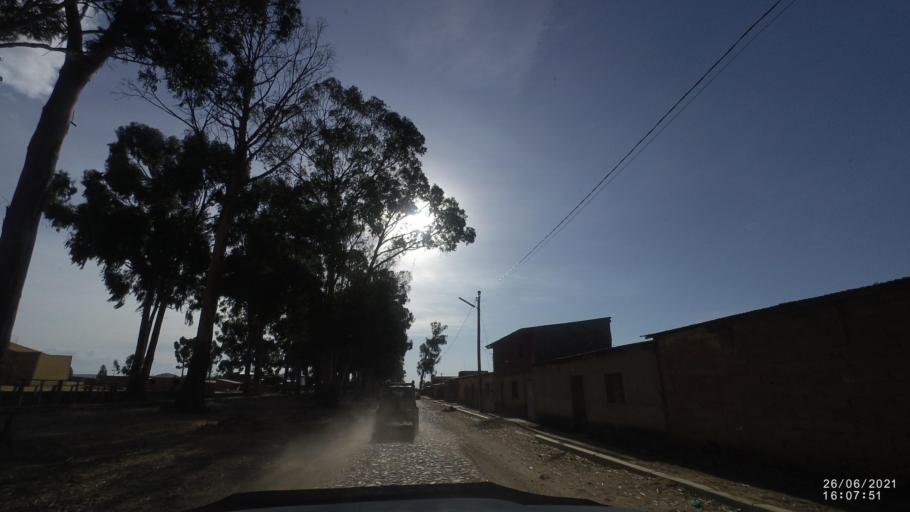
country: BO
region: Cochabamba
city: Arani
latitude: -17.8194
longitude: -65.7760
